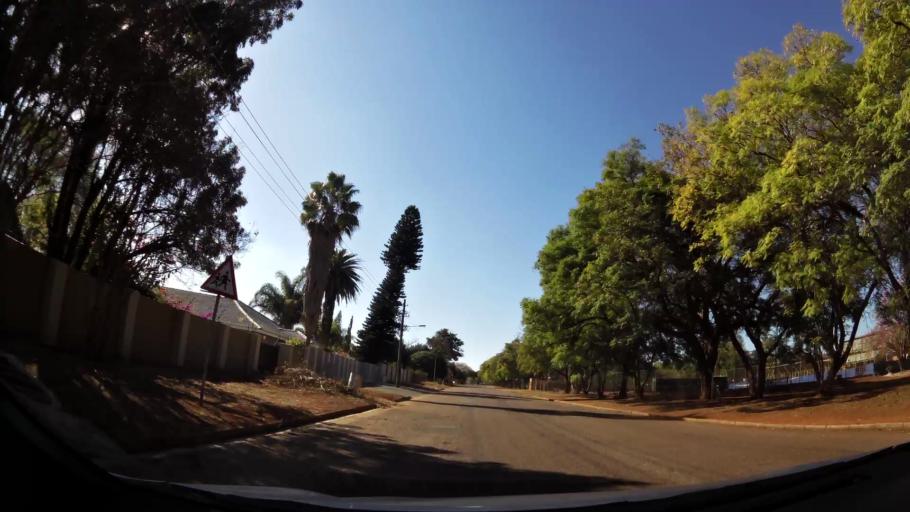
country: ZA
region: Limpopo
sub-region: Waterberg District Municipality
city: Mokopane
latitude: -24.1860
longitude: 29.0030
